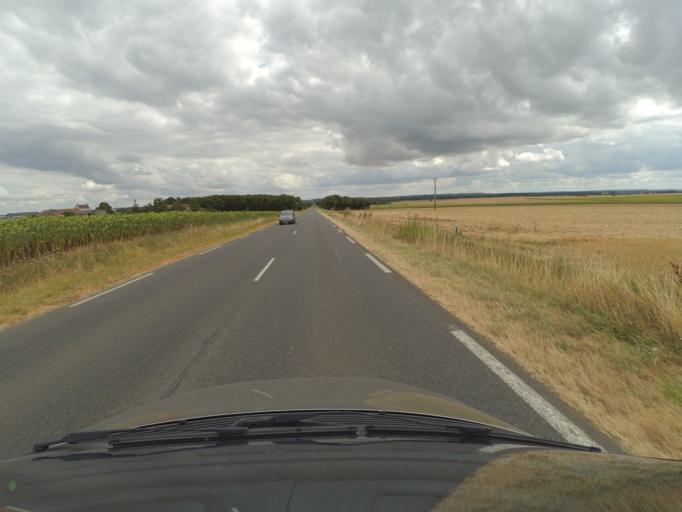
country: FR
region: Centre
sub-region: Departement d'Indre-et-Loire
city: Richelieu
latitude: 47.0099
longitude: 0.2904
